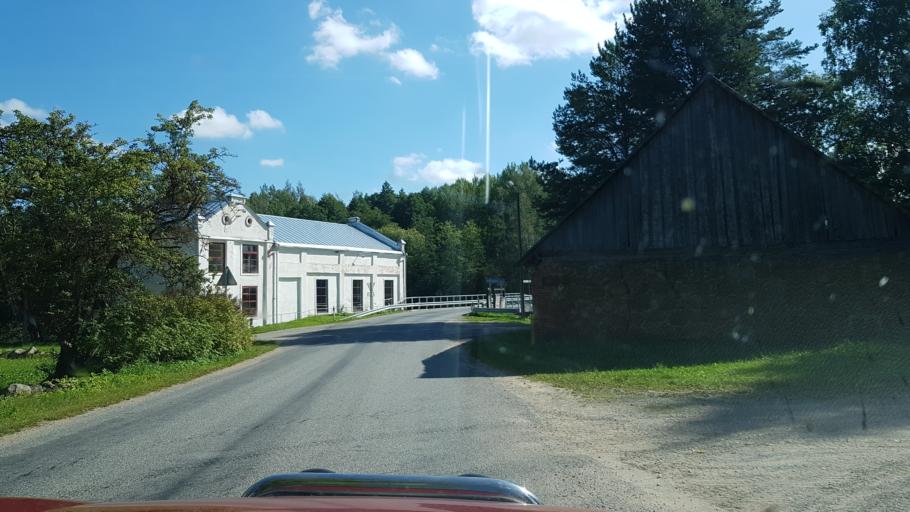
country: EE
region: Polvamaa
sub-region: Raepina vald
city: Rapina
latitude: 58.0905
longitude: 27.3450
